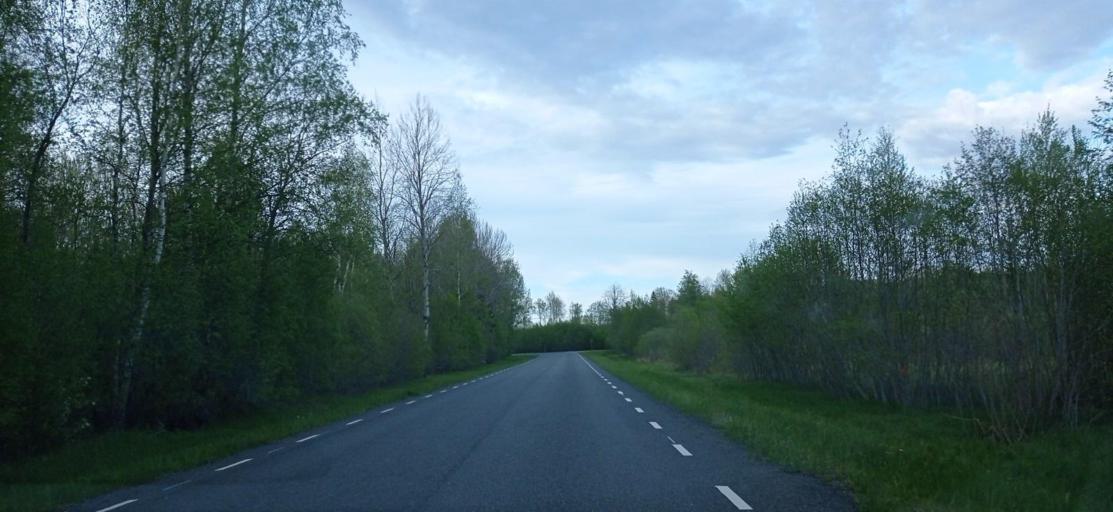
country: EE
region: Paernumaa
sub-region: Tootsi vald
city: Tootsi
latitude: 58.5648
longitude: 24.8067
